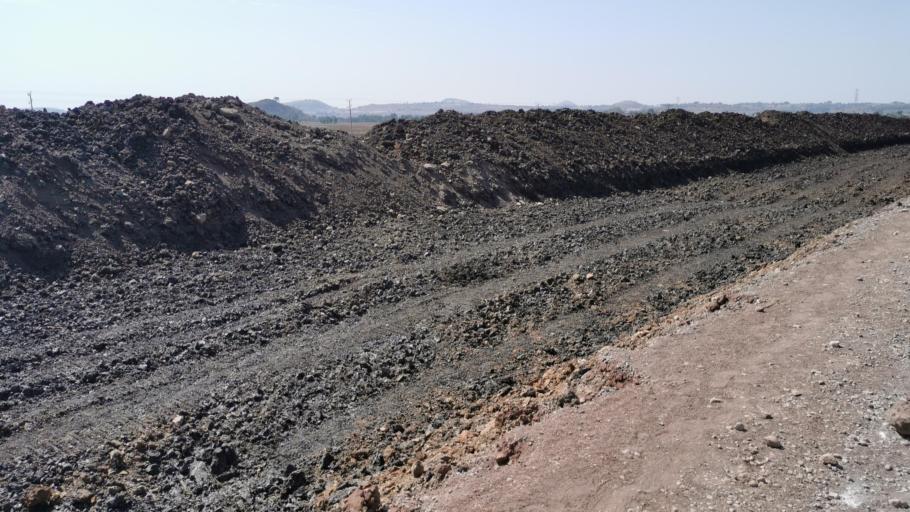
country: ET
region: Amhara
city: Bahir Dar
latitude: 11.8404
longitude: 37.0017
